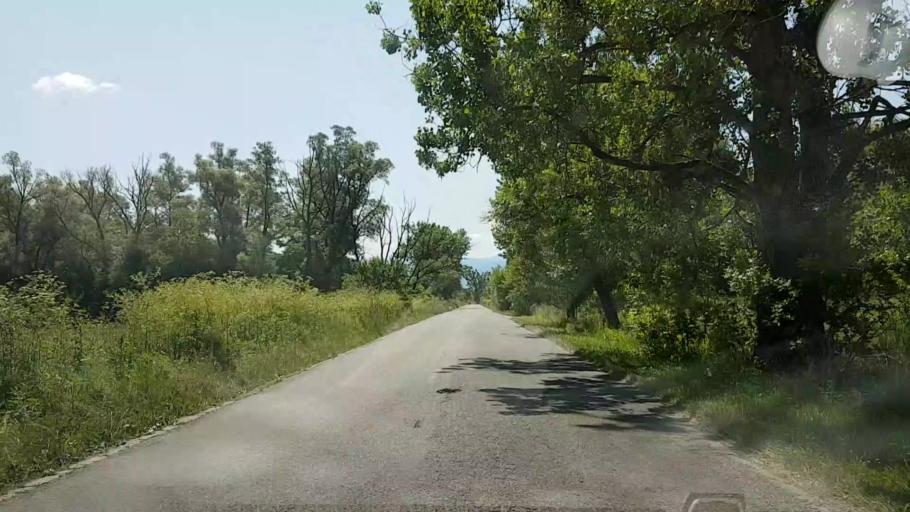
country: RO
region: Brasov
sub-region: Comuna Voila
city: Voila
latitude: 45.8562
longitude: 24.8293
